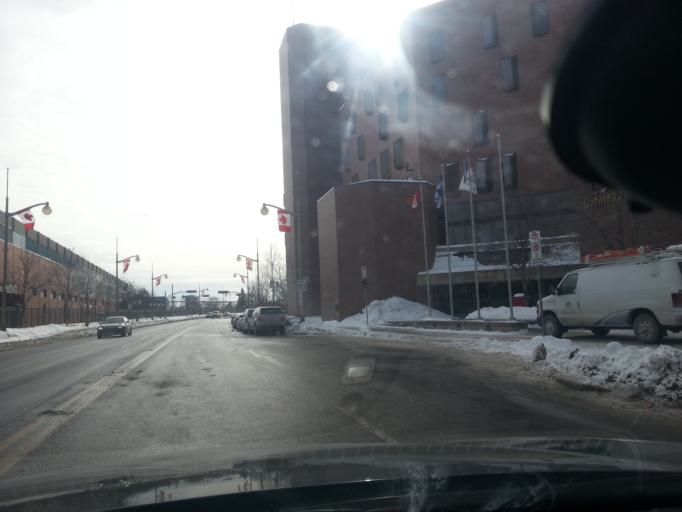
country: CA
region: Ontario
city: Ottawa
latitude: 45.4284
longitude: -75.7104
